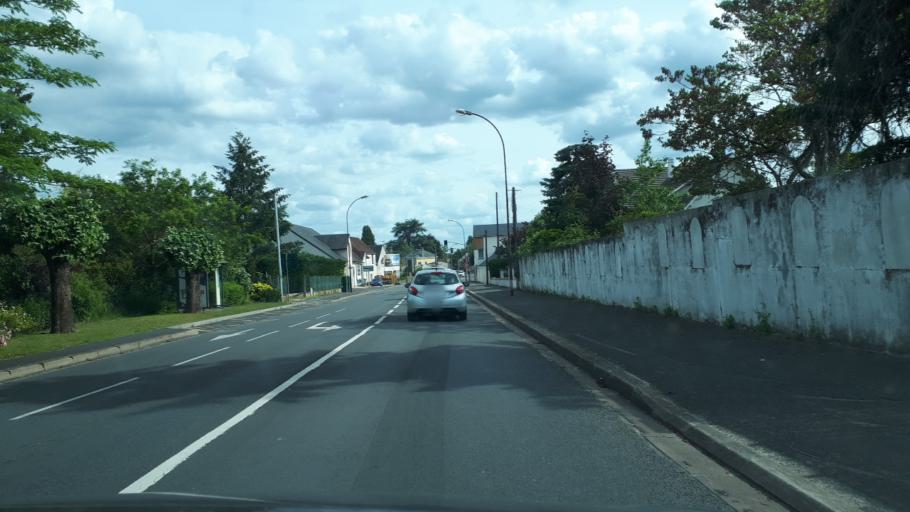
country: FR
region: Centre
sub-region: Departement du Loir-et-Cher
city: Romorantin-Lanthenay
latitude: 47.3612
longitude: 1.7393
